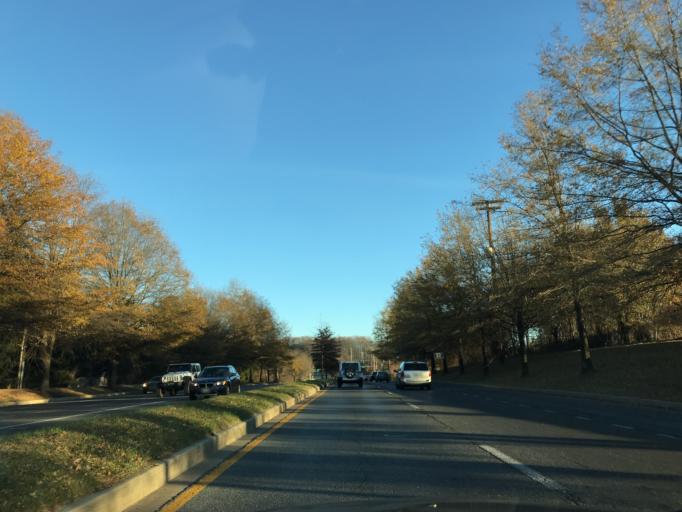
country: US
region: Maryland
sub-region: Montgomery County
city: Olney
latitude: 39.1464
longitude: -77.0505
